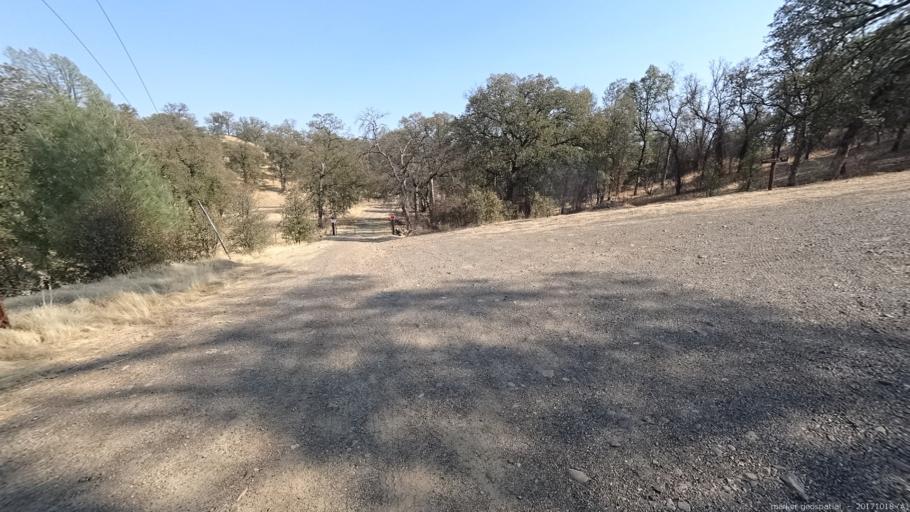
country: US
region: California
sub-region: Shasta County
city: Palo Cedro
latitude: 40.5552
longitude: -122.2499
